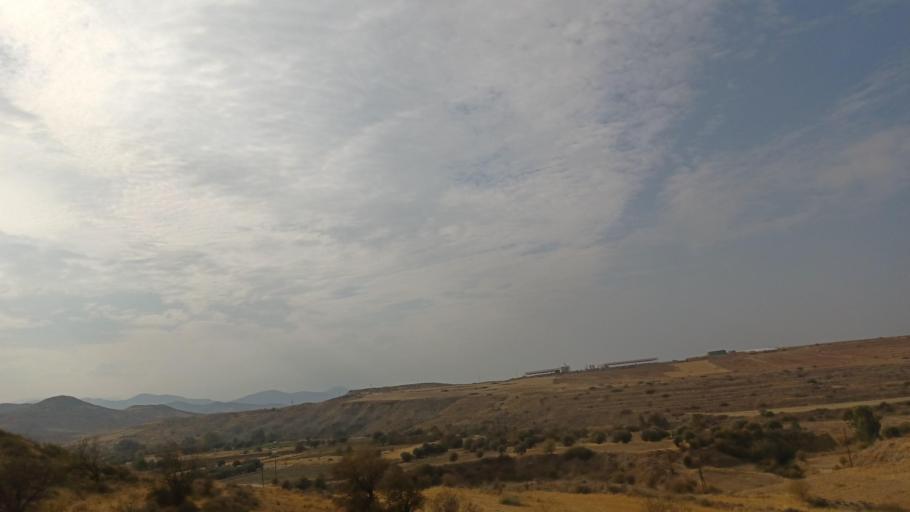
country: CY
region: Lefkosia
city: Peristerona
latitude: 35.0779
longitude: 33.0922
